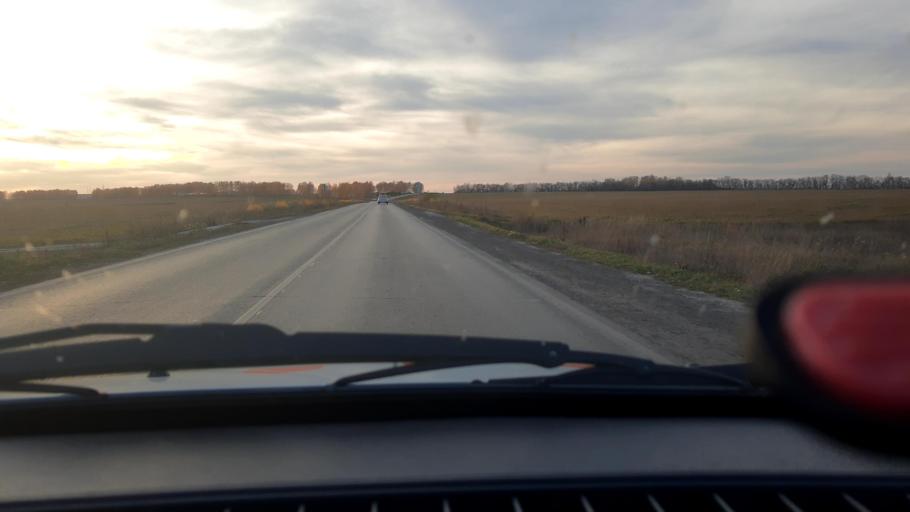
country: RU
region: Bashkortostan
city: Aksakovo
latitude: 54.0086
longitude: 54.3687
